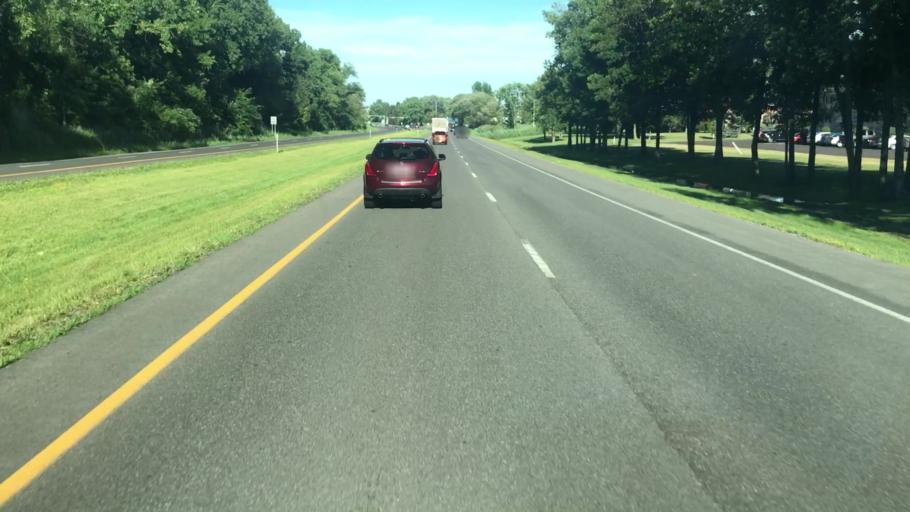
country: US
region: New York
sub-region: Onondaga County
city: Liverpool
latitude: 43.1313
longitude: -76.2269
